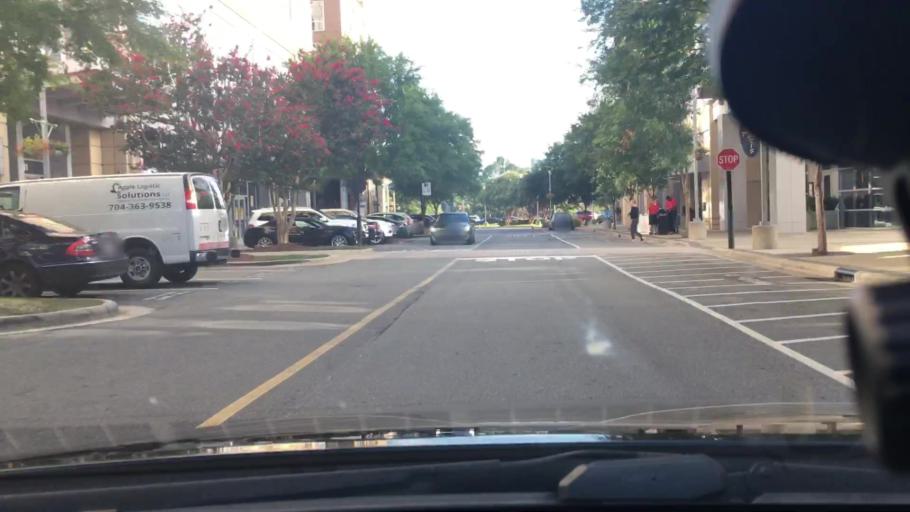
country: US
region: North Carolina
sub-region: Mecklenburg County
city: Charlotte
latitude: 35.2128
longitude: -80.8354
